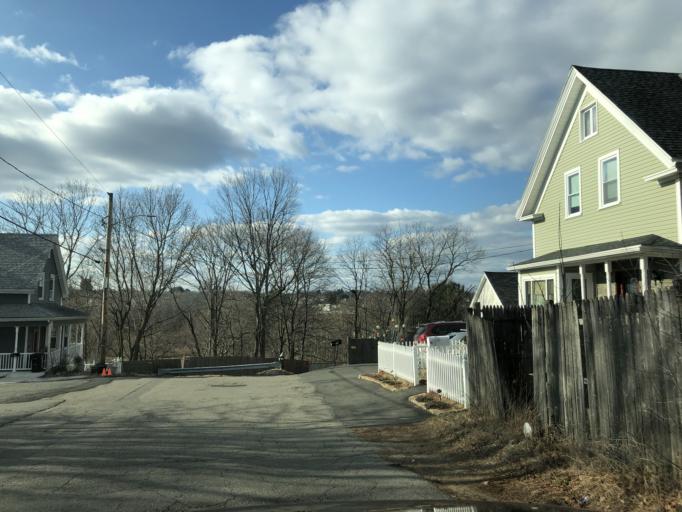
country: US
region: Massachusetts
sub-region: Plymouth County
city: Brockton
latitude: 42.1000
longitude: -71.0115
